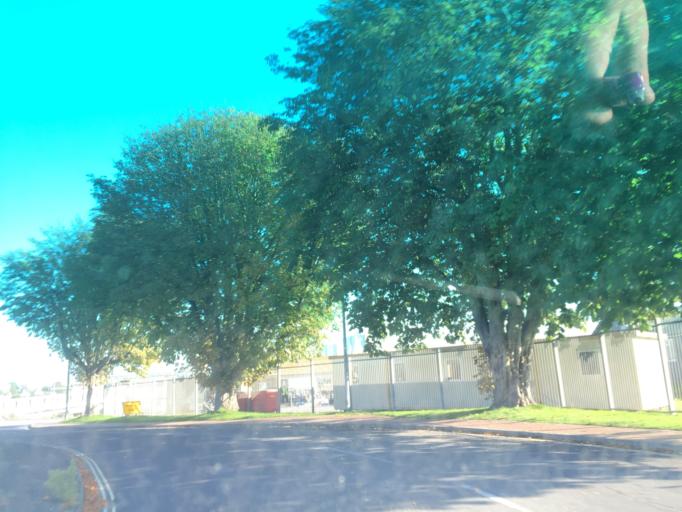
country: GB
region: England
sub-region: Hampshire
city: Gosport
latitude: 50.7883
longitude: -1.1229
